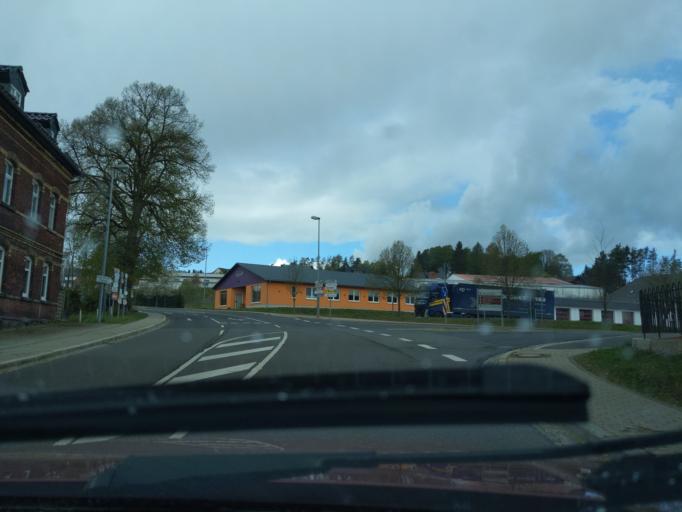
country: DE
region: Saxony
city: Schoenheide
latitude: 50.5050
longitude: 12.5223
